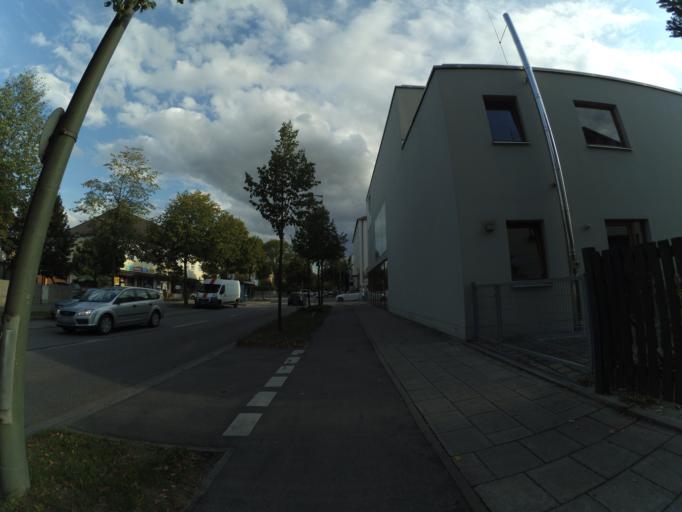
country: DE
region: Bavaria
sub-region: Upper Bavaria
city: Oberschleissheim
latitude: 48.1973
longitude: 11.5452
